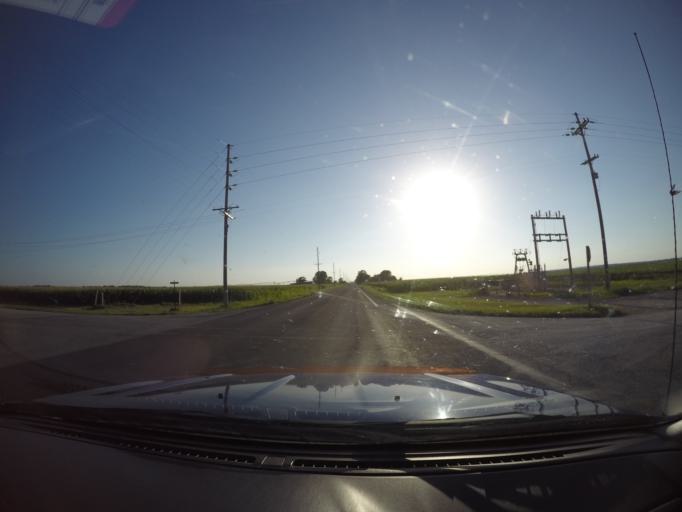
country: US
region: Kansas
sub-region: Pottawatomie County
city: Saint Marys
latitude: 39.2166
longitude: -96.1473
